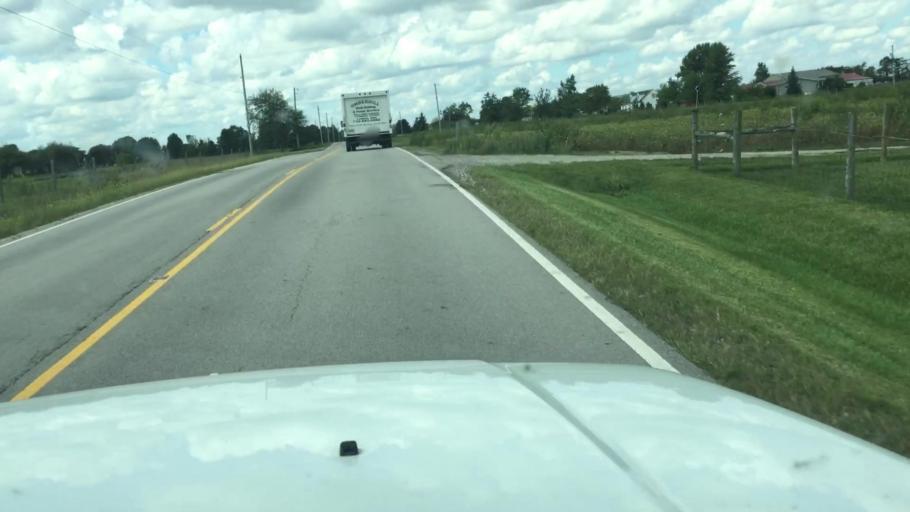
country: US
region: Ohio
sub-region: Madison County
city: London
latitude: 39.8290
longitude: -83.3669
